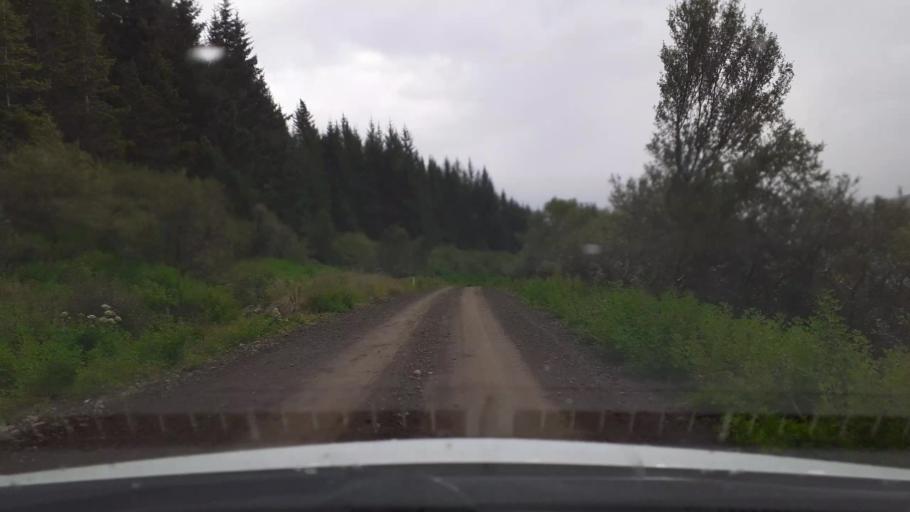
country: IS
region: Capital Region
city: Mosfellsbaer
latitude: 64.5164
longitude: -21.4166
